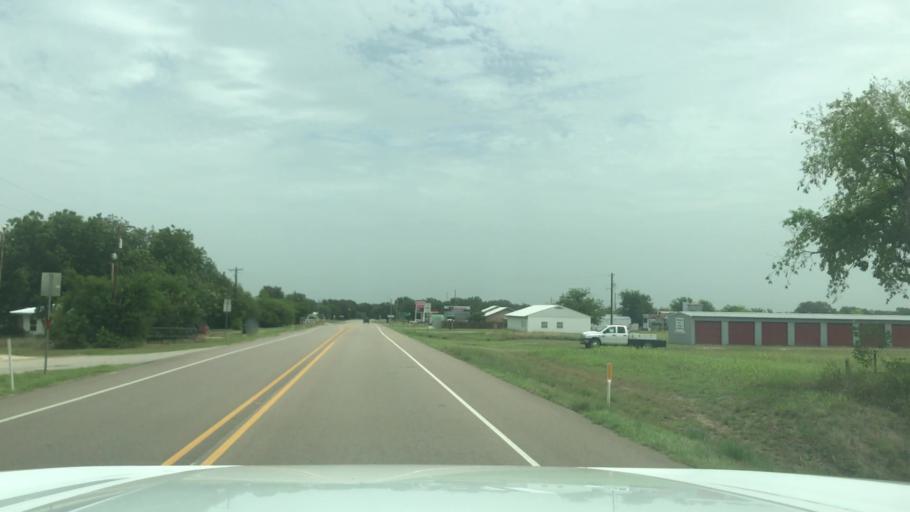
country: US
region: Texas
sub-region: Hamilton County
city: Hico
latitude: 31.9799
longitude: -97.8731
